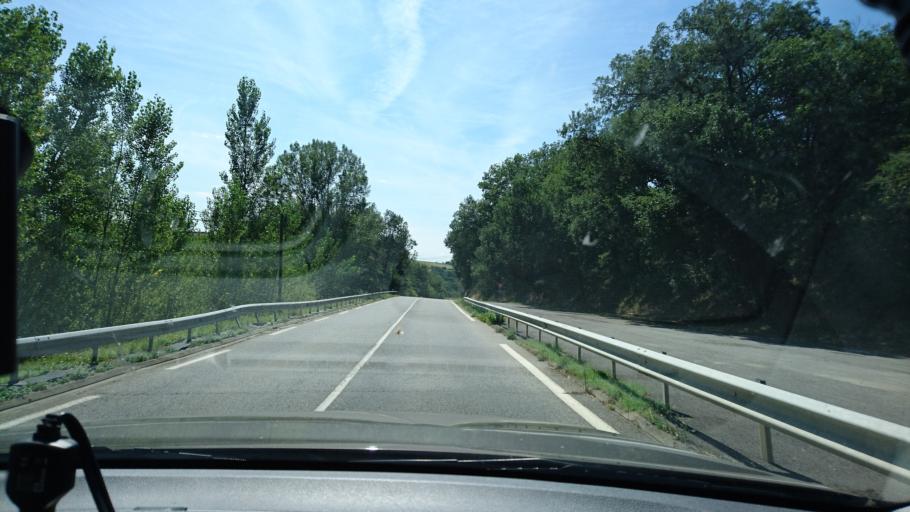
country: FR
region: Midi-Pyrenees
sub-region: Departement de la Haute-Garonne
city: Noe
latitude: 43.3396
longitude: 1.2829
